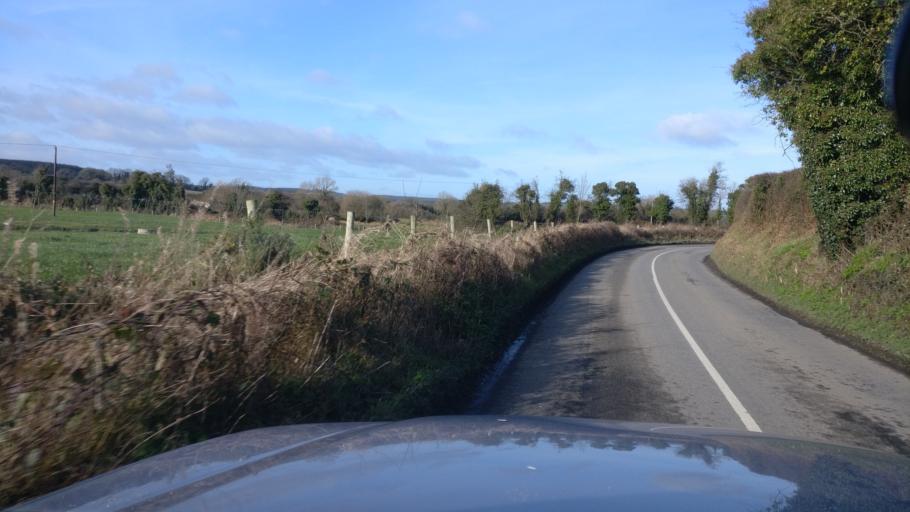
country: IE
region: Leinster
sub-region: Kilkenny
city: Castlecomer
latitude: 52.8799
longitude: -7.1635
